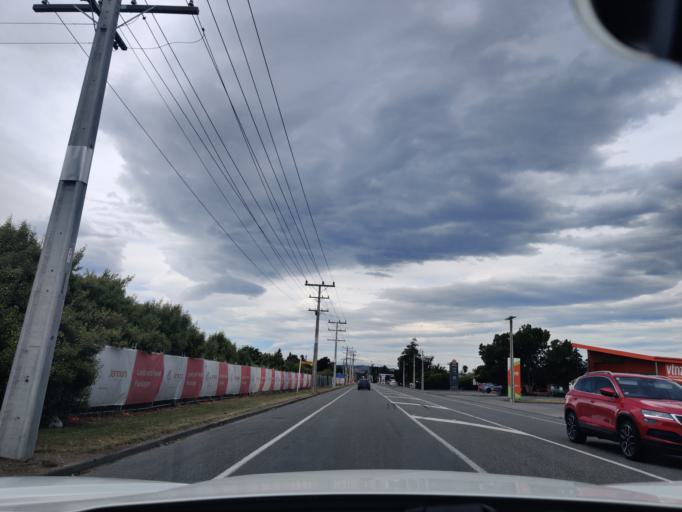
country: NZ
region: Wellington
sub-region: Masterton District
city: Masterton
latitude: -40.9478
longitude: 175.6352
